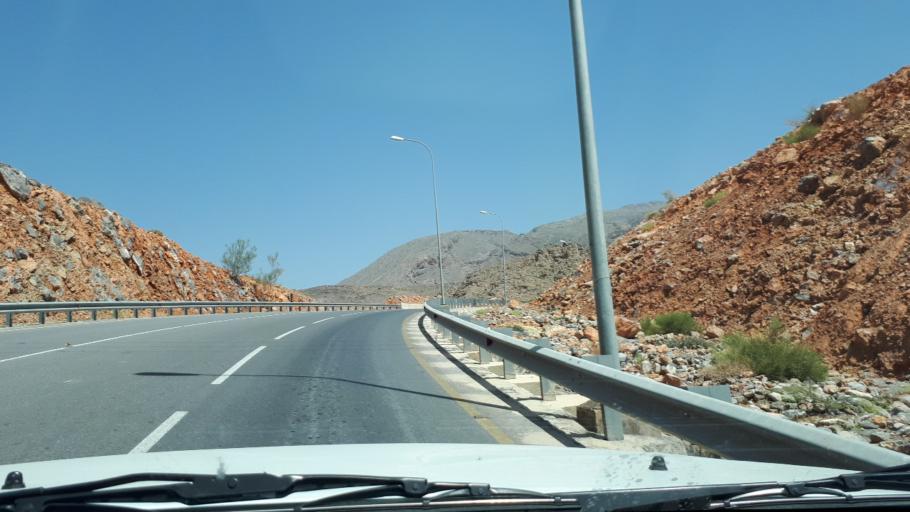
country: OM
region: Muhafazat ad Dakhiliyah
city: Izki
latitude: 22.9750
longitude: 57.6992
